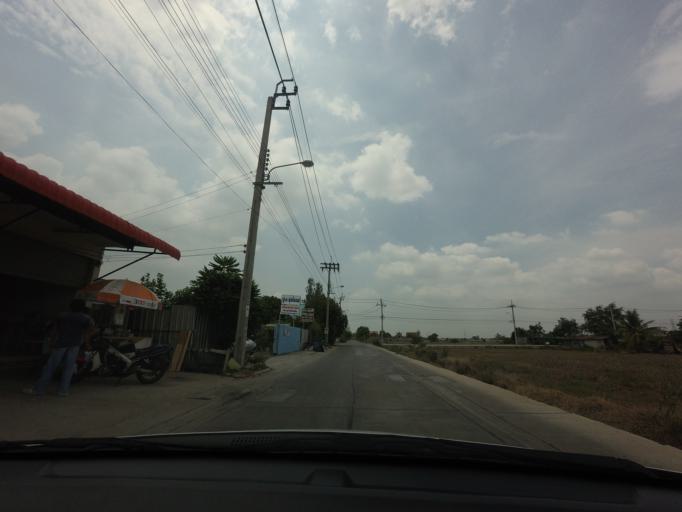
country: TH
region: Pathum Thani
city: Lam Luk Ka
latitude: 13.8934
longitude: 100.7035
